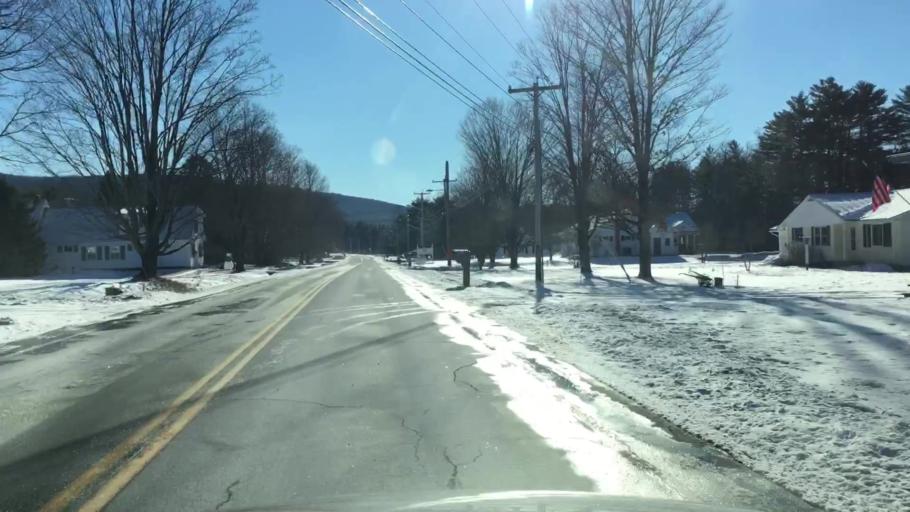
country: US
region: New Hampshire
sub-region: Grafton County
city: Woodsville
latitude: 44.2574
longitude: -72.0522
